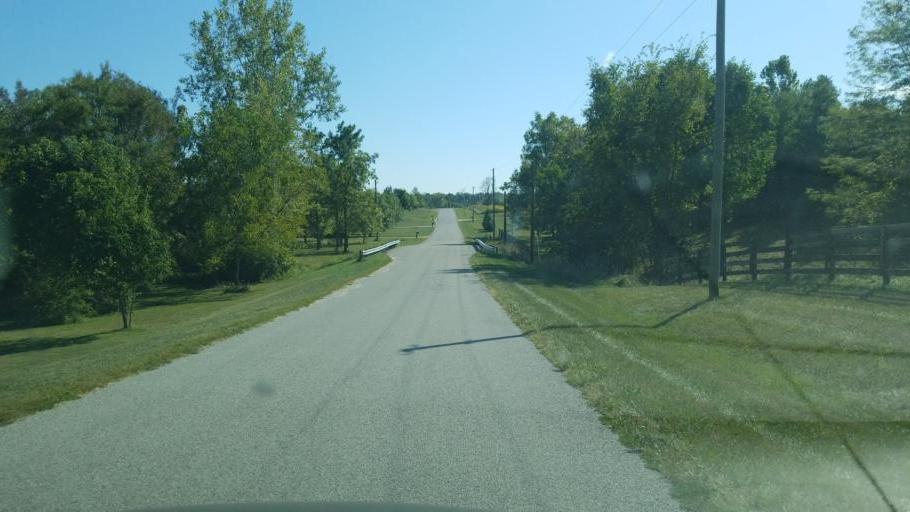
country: US
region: Ohio
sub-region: Champaign County
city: Mechanicsburg
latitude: 40.1222
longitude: -83.6008
